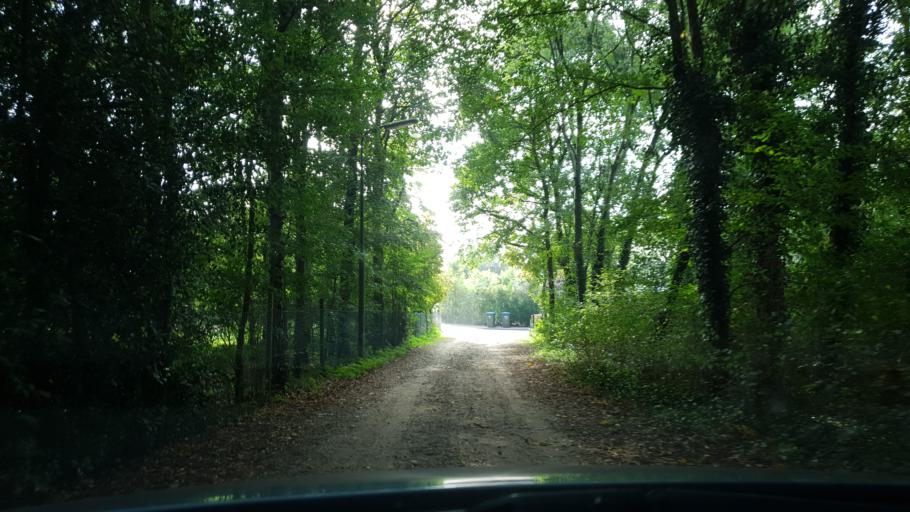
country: NL
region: Gelderland
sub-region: Gemeente Wijchen
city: Bergharen
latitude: 51.8549
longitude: 5.6745
